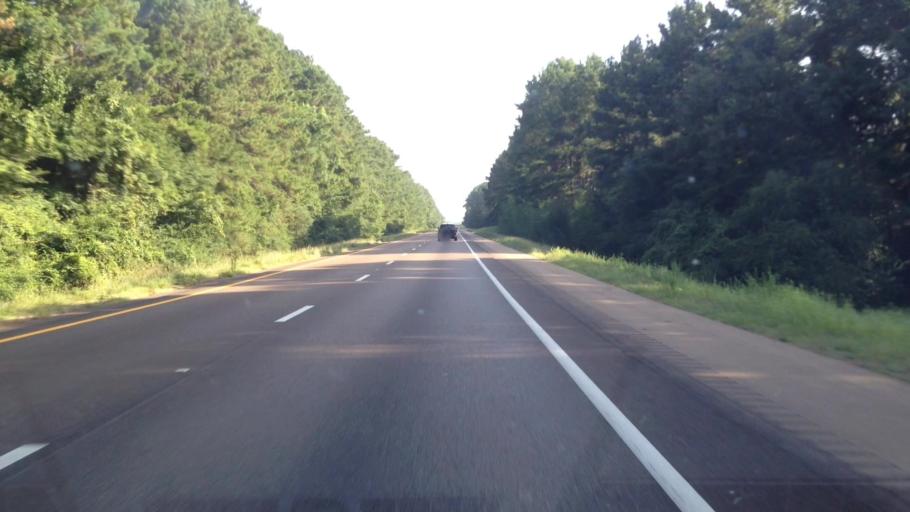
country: US
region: Mississippi
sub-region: Pike County
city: Summit
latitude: 31.3385
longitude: -90.4776
